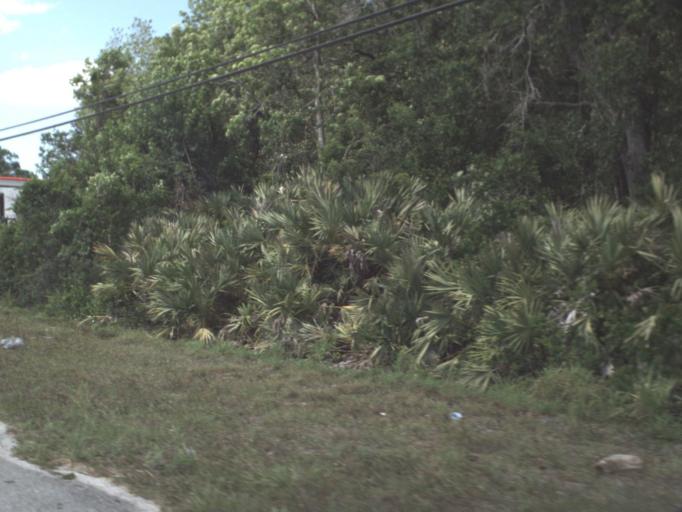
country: US
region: Florida
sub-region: Brevard County
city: Mims
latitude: 28.6490
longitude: -80.8369
